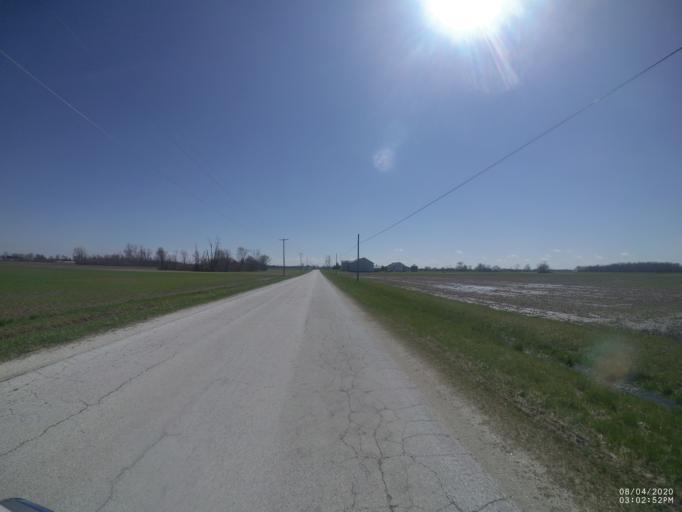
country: US
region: Ohio
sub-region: Sandusky County
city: Stony Prairie
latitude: 41.3331
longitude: -83.2396
